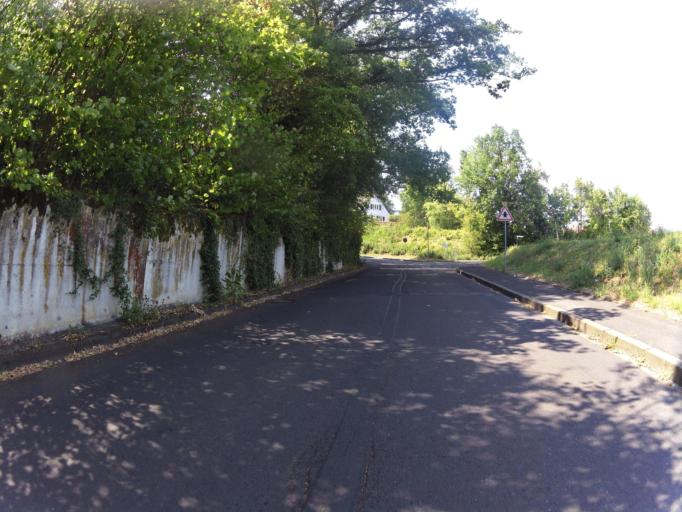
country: DE
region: Bavaria
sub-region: Regierungsbezirk Unterfranken
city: Ochsenfurt
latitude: 49.6625
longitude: 10.0591
